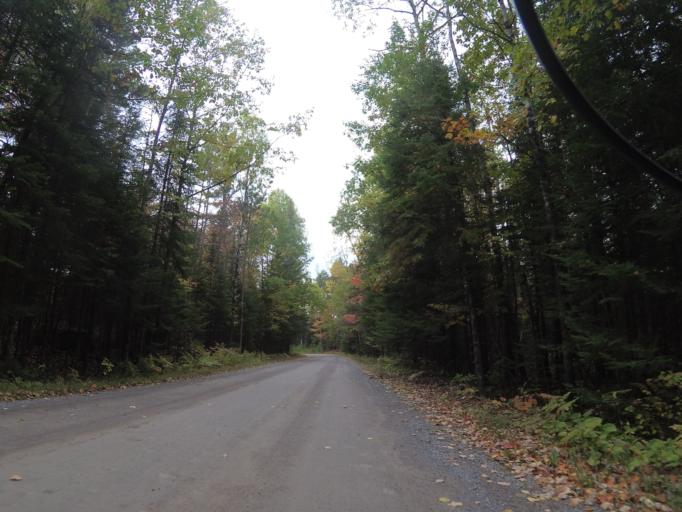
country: CA
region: Ontario
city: Renfrew
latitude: 45.2604
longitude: -77.1977
